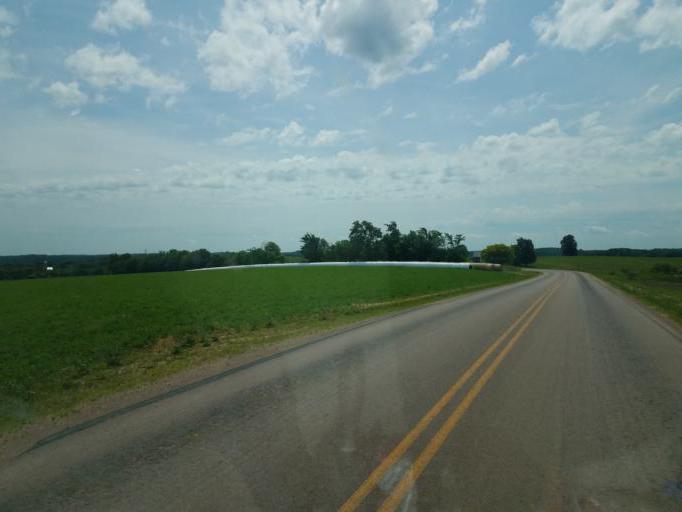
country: US
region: Wisconsin
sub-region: Vernon County
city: Hillsboro
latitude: 43.6086
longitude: -90.4371
